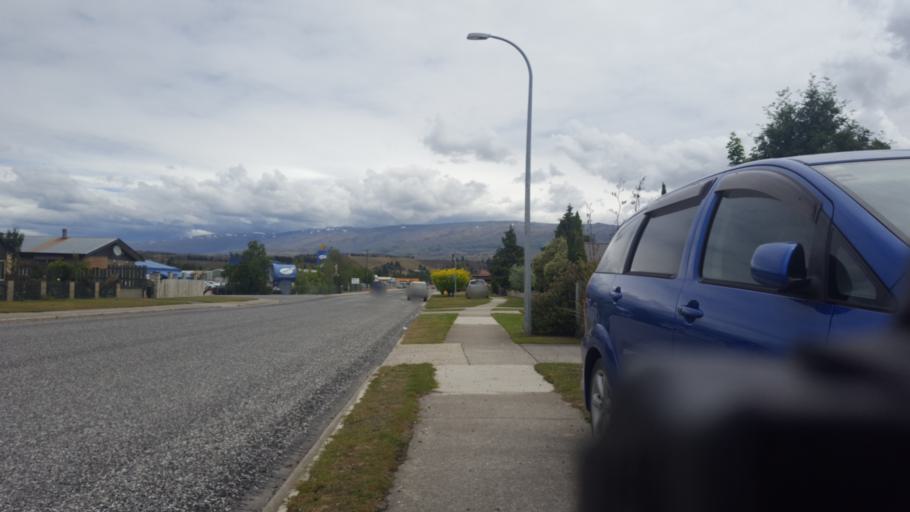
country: NZ
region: Otago
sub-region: Queenstown-Lakes District
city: Wanaka
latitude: -45.2455
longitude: 169.3770
